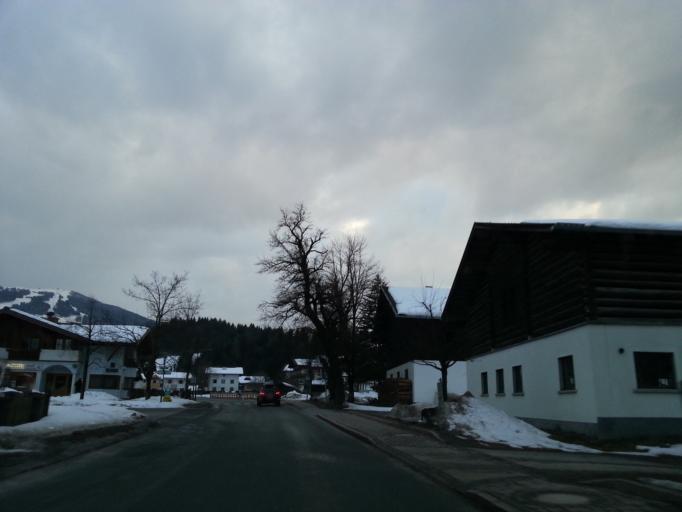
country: AT
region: Salzburg
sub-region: Politischer Bezirk Sankt Johann im Pongau
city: Flachau
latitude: 47.3725
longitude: 13.3888
